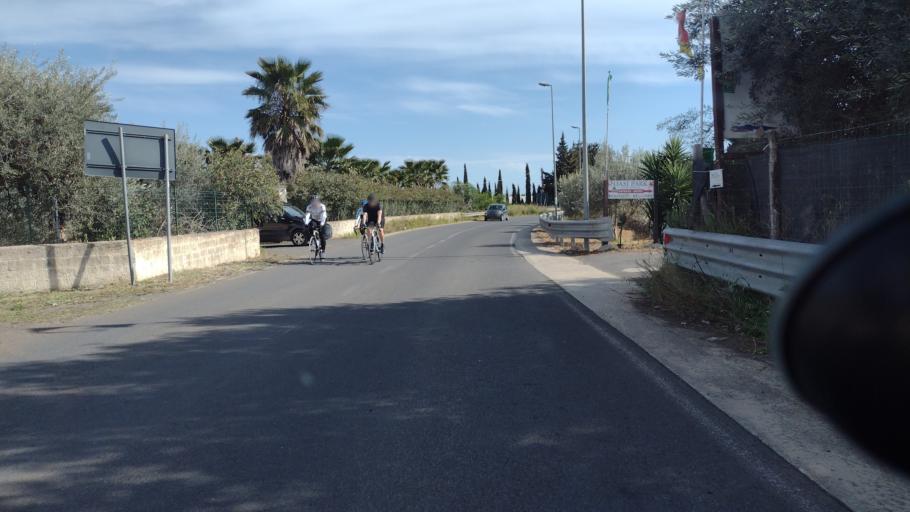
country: IT
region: Sicily
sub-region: Provincia di Siracusa
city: Avola
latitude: 36.8700
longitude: 15.1288
